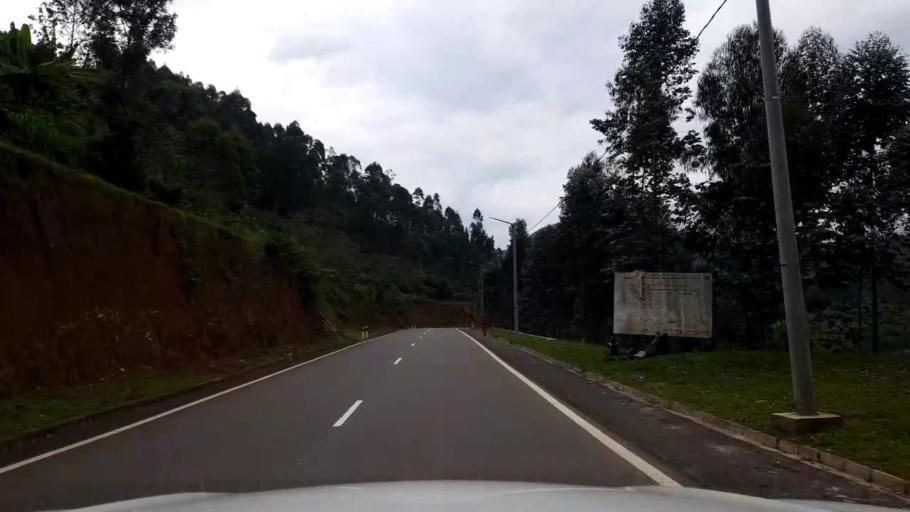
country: RW
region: Western Province
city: Kibuye
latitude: -1.9214
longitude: 29.3695
